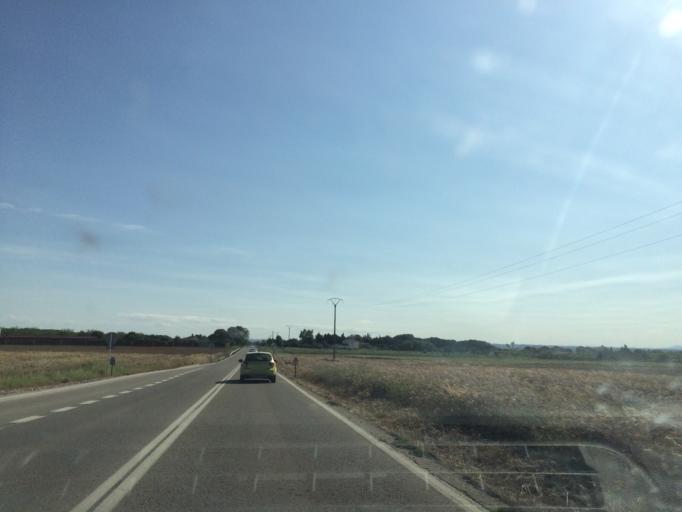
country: ES
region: Madrid
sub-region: Provincia de Madrid
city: Fuente el Saz
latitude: 40.6605
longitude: -3.4874
